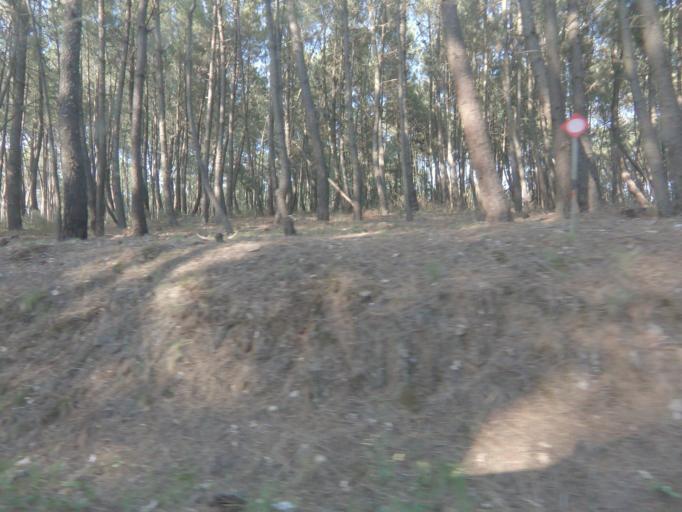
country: PT
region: Vila Real
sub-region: Vila Real
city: Vila Real
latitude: 41.2775
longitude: -7.6815
